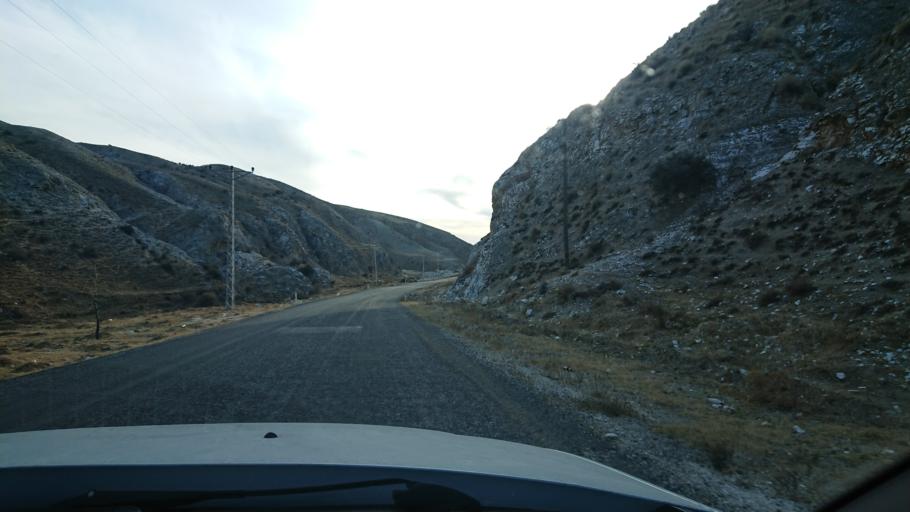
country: TR
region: Ankara
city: Sereflikochisar
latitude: 38.7529
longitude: 33.6920
